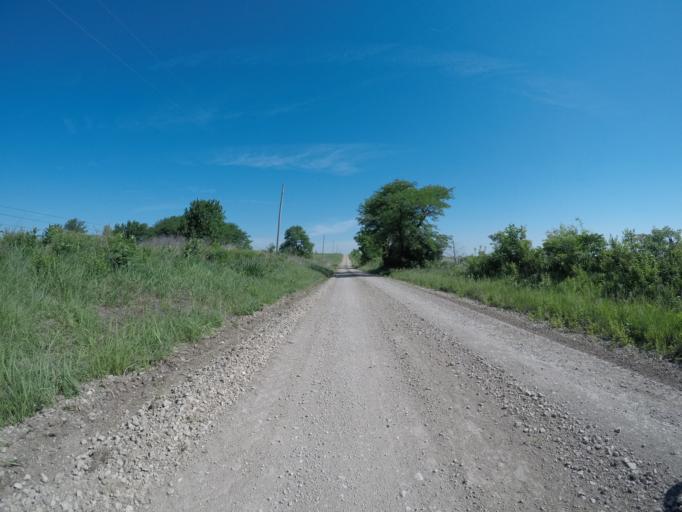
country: US
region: Kansas
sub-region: Wabaunsee County
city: Alma
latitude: 38.9503
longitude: -96.1138
